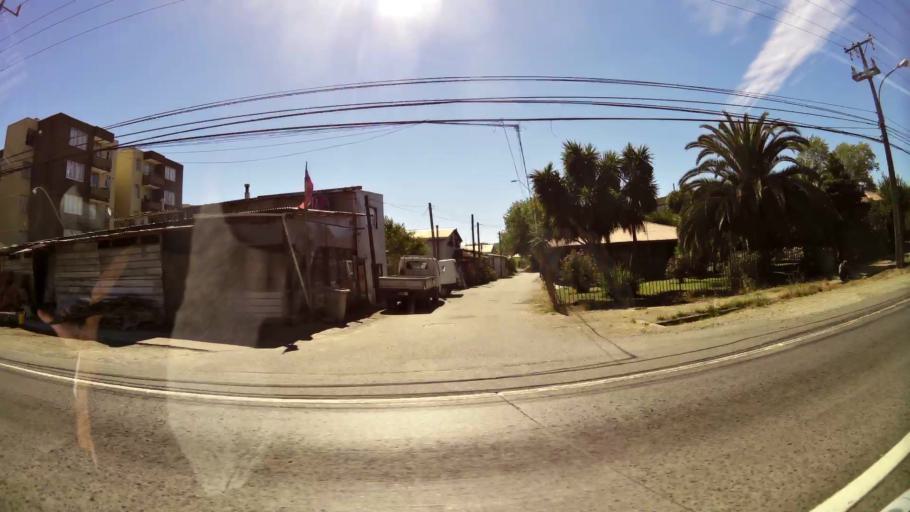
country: CL
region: Biobio
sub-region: Provincia de Concepcion
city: Penco
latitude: -36.7795
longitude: -73.0195
